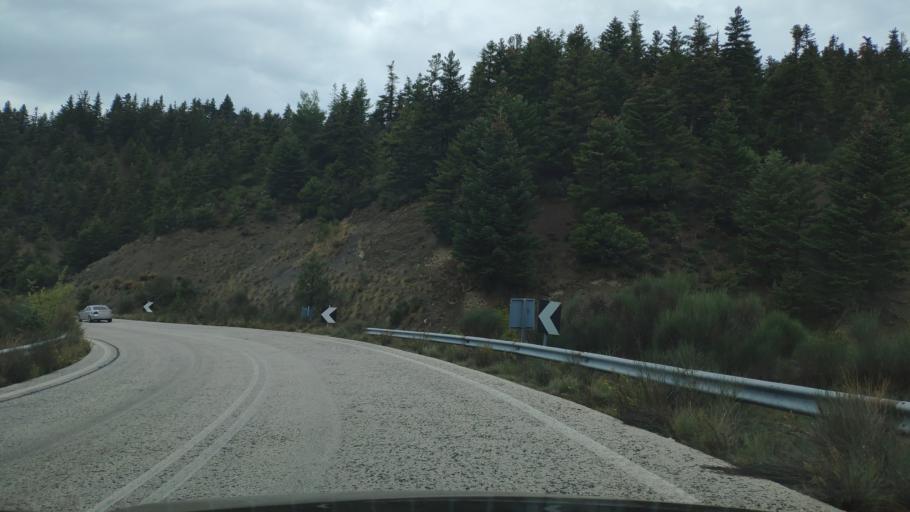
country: GR
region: Peloponnese
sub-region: Nomos Arkadias
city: Dimitsana
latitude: 37.6398
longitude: 22.0918
